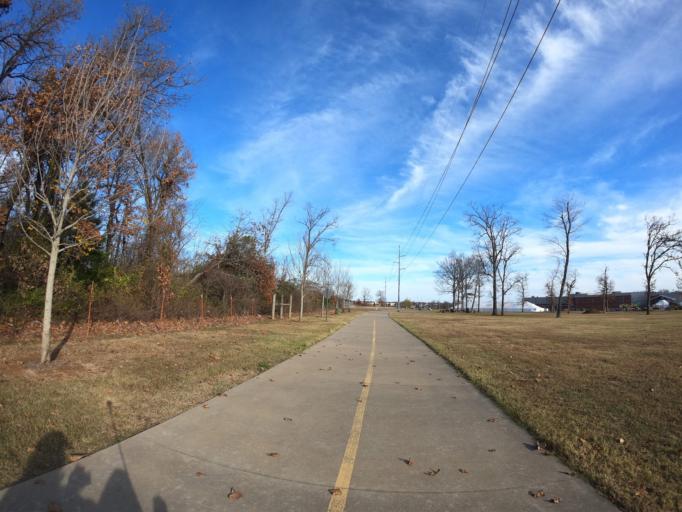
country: US
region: Arkansas
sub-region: Benton County
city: Lowell
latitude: 36.2811
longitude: -94.1692
